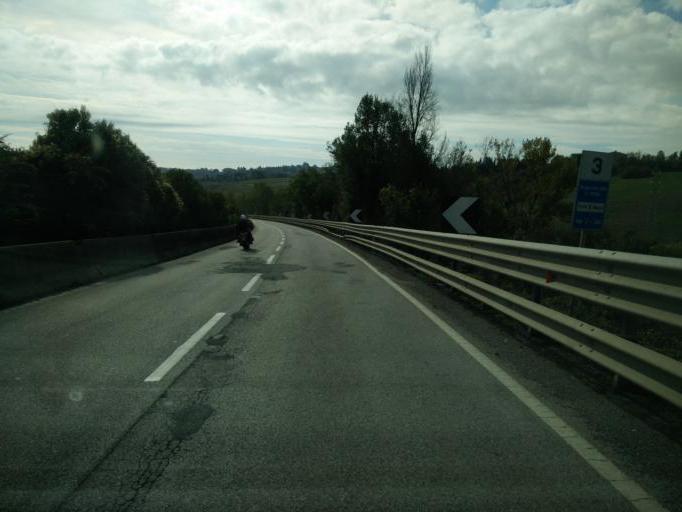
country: IT
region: Tuscany
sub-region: Provincia di Siena
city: Belverde
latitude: 43.3336
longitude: 11.2914
